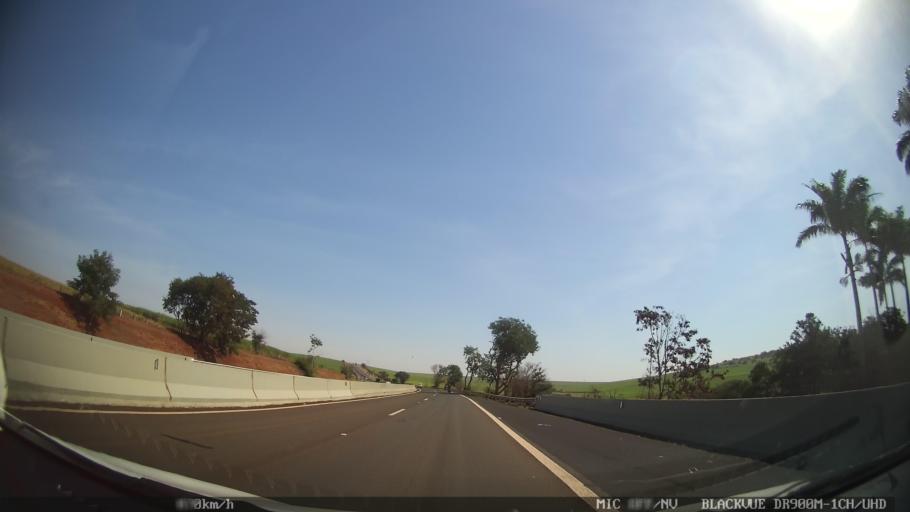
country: BR
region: Sao Paulo
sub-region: Ribeirao Preto
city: Ribeirao Preto
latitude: -21.1662
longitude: -47.8756
